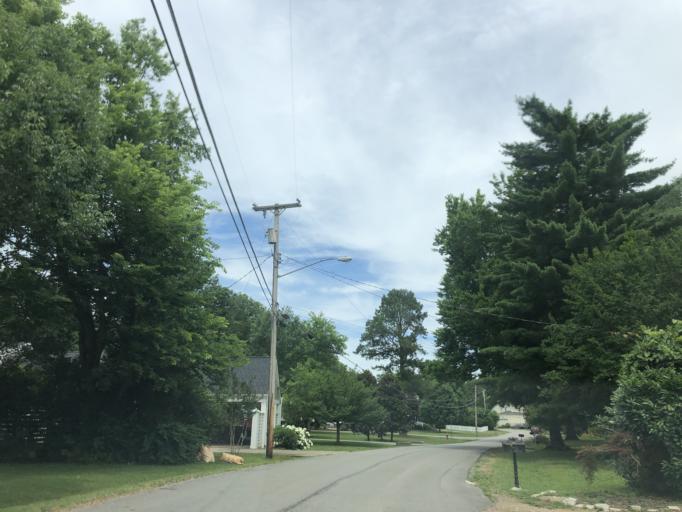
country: US
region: Tennessee
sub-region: Davidson County
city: Oak Hill
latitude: 36.1087
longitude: -86.7851
